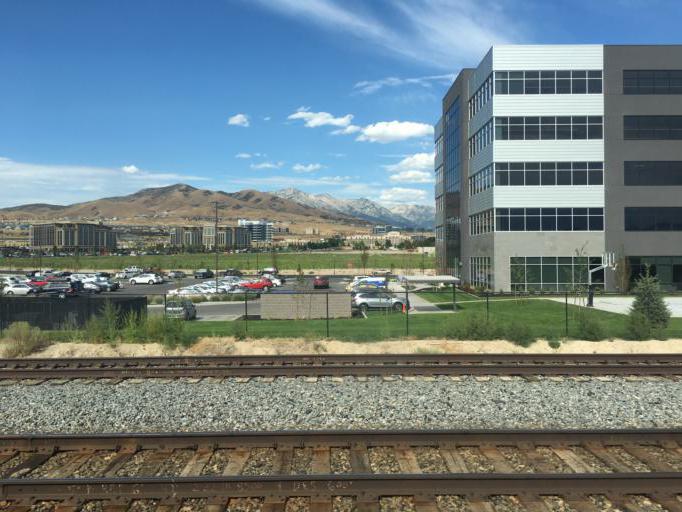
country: US
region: Utah
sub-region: Utah County
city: Lehi
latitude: 40.4237
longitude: -111.8945
